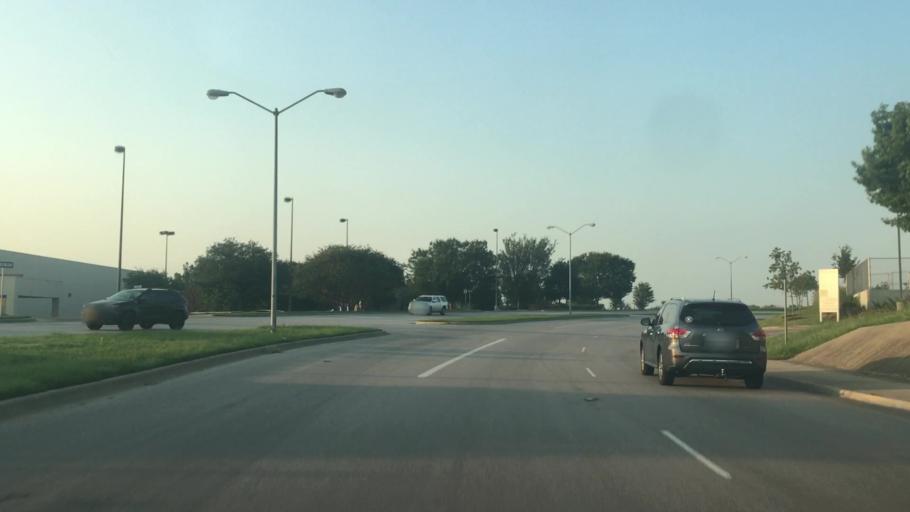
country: US
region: Texas
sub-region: Travis County
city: Windemere
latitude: 30.4817
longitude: -97.6603
